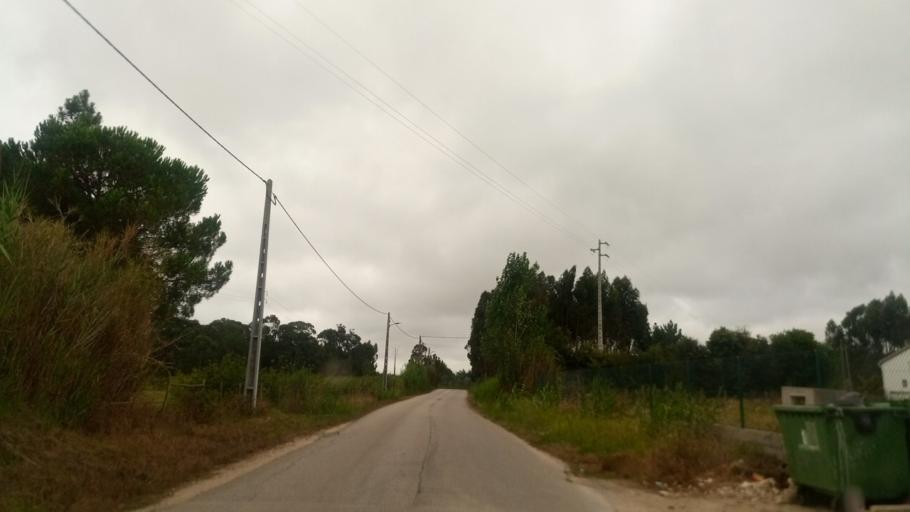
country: PT
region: Leiria
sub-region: Caldas da Rainha
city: Caldas da Rainha
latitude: 39.4187
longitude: -9.1401
